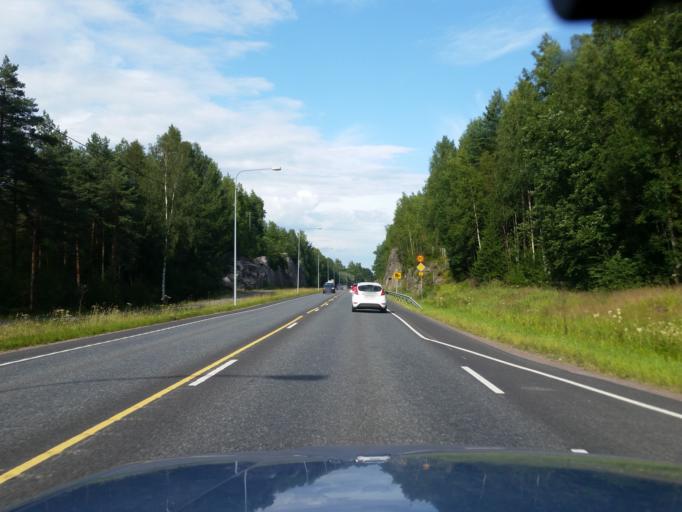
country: FI
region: Uusimaa
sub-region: Helsinki
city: Kirkkonummi
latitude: 60.1062
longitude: 24.3715
